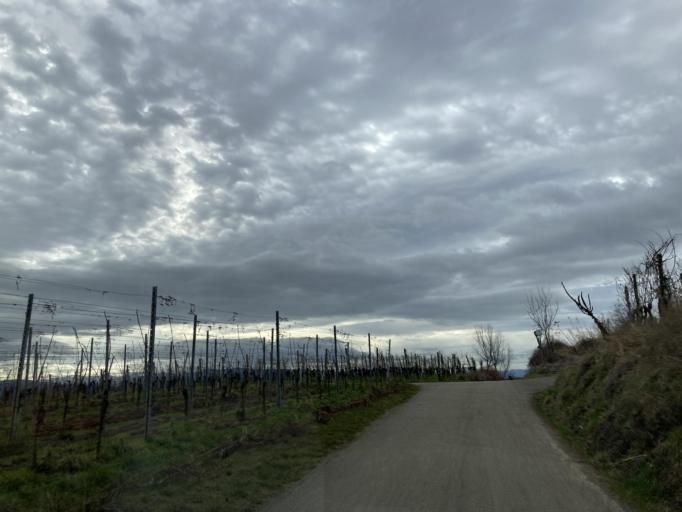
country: DE
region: Baden-Wuerttemberg
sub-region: Freiburg Region
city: Bahlingen
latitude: 48.1174
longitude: 7.7132
